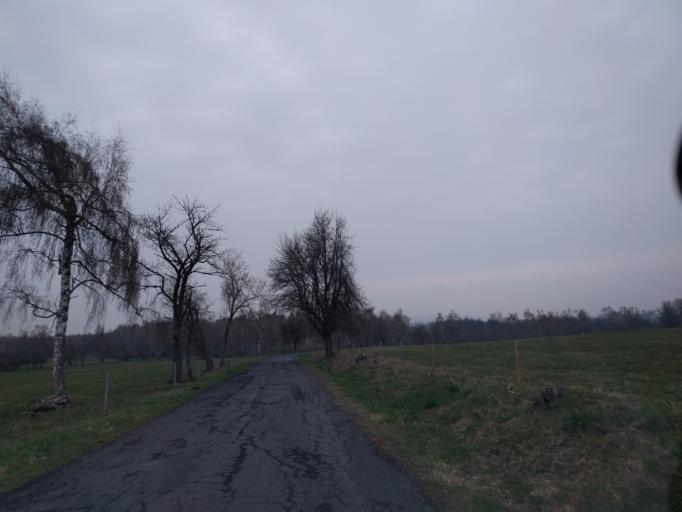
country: CZ
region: Karlovarsky
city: Bochov
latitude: 50.1246
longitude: 13.0845
